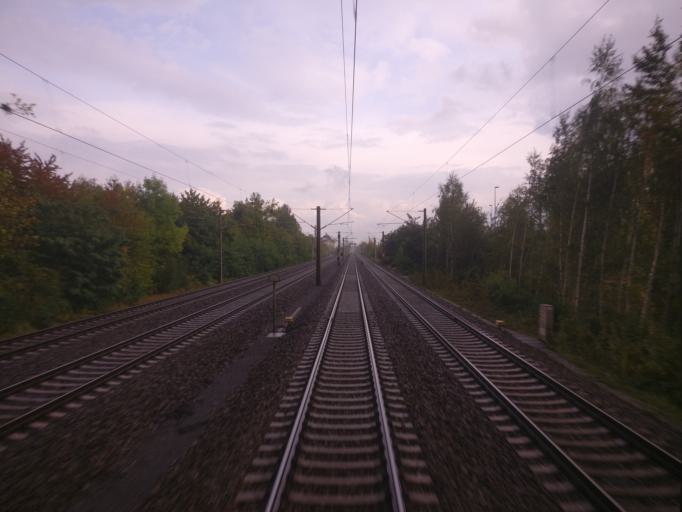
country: DE
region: Saxony
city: Dresden
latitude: 51.0151
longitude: 13.8027
